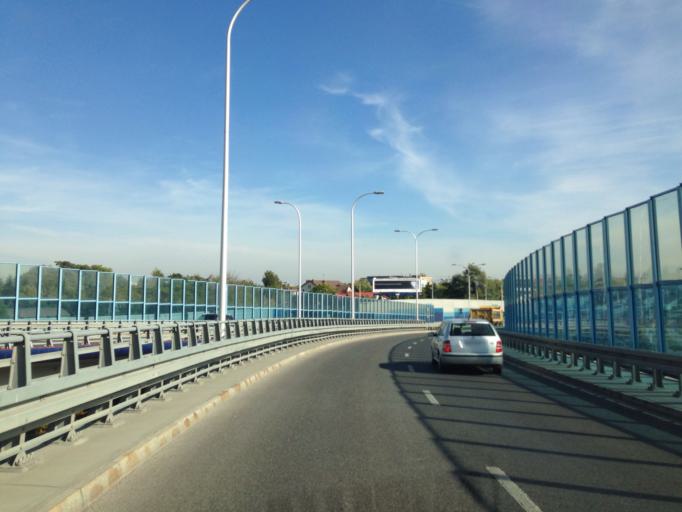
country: PL
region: Masovian Voivodeship
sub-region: Warszawa
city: Wlochy
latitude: 52.1957
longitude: 20.9288
